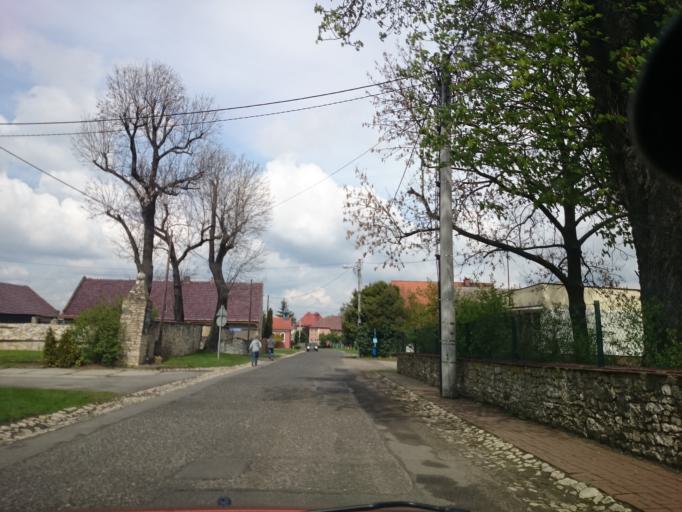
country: PL
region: Opole Voivodeship
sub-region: Powiat krapkowicki
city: Rozwadza
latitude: 50.4904
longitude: 18.1207
